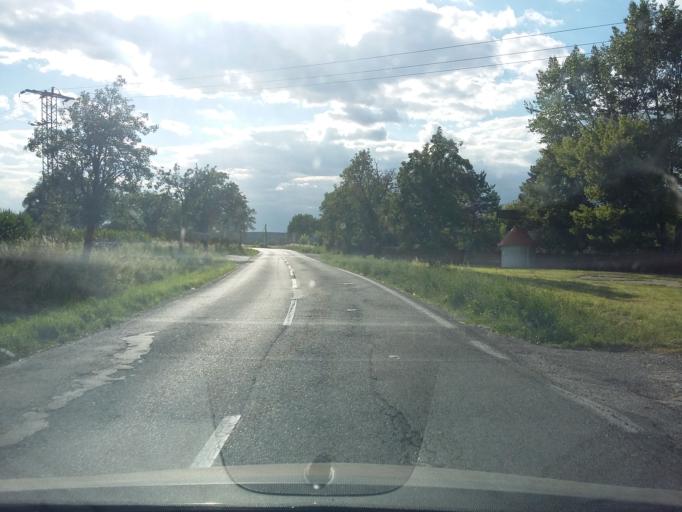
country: SK
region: Trnavsky
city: Smolenice
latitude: 48.5156
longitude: 17.2940
